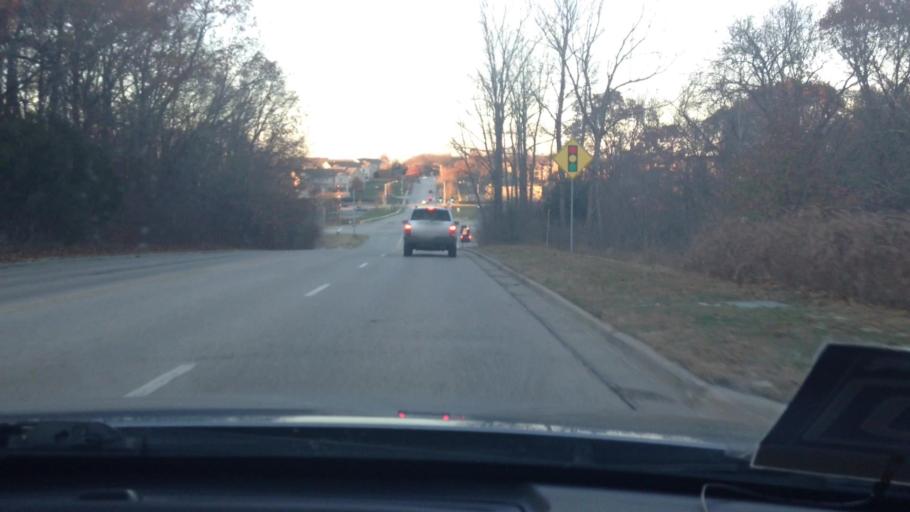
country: US
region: Kansas
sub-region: Wyandotte County
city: Bonner Springs
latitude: 39.1139
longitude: -94.8815
